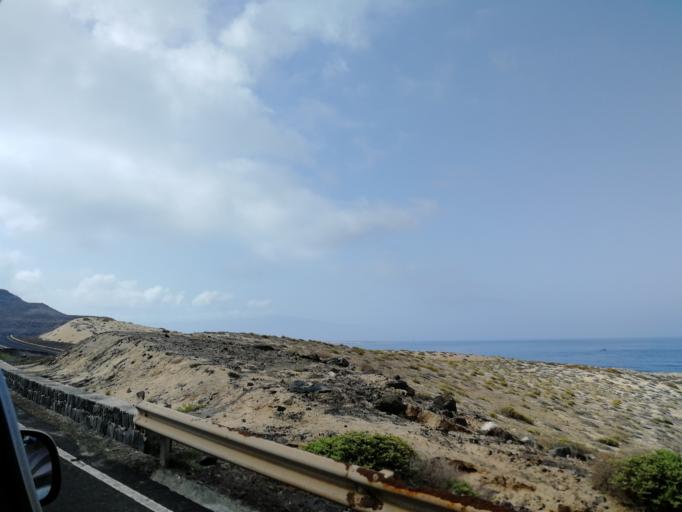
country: CV
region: Sao Vicente
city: Mindelo
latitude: 16.8602
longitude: -24.8903
